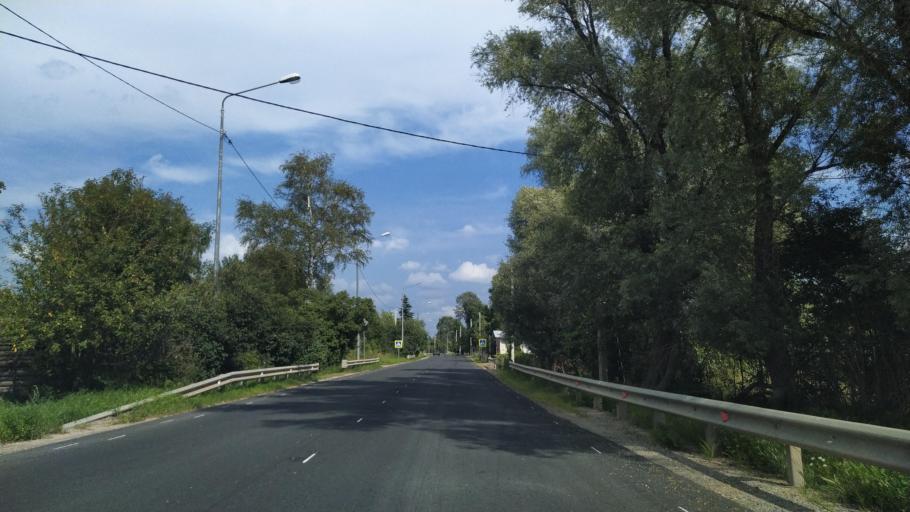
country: RU
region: Pskov
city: Porkhov
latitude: 57.7422
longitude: 29.0326
